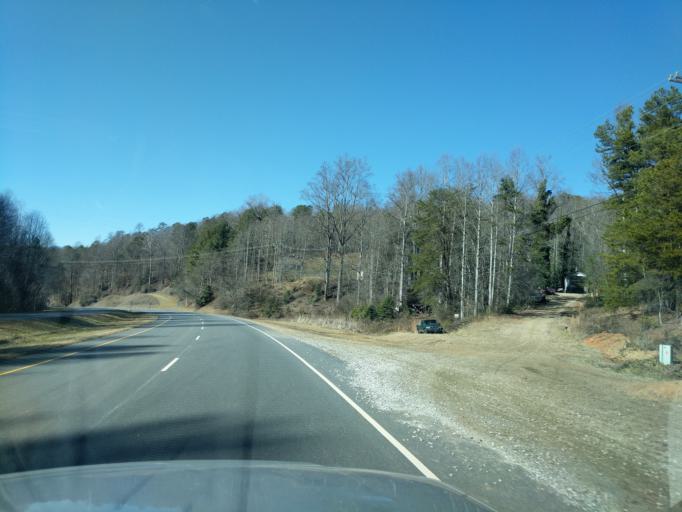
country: US
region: North Carolina
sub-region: Swain County
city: Bryson City
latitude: 35.3743
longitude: -83.5110
